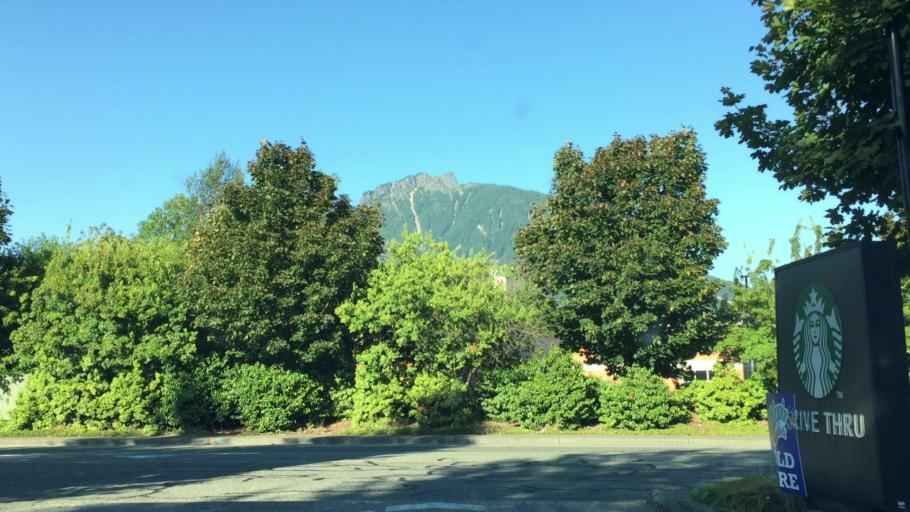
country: US
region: Washington
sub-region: King County
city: North Bend
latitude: 47.4878
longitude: -121.7937
